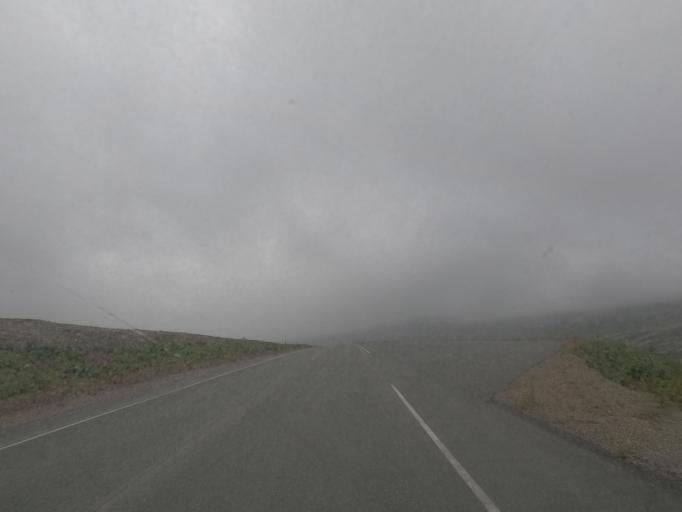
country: US
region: Alaska
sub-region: Haines Borough
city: Haines
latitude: 59.6782
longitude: -136.5715
